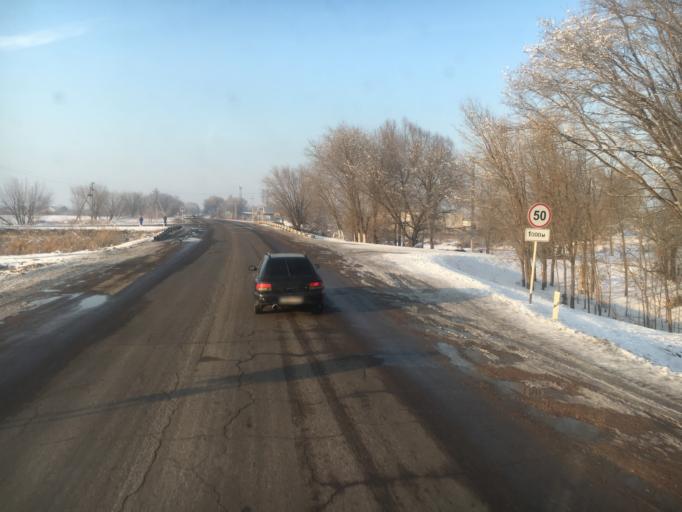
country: KZ
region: Almaty Oblysy
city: Burunday
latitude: 43.3315
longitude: 76.6619
